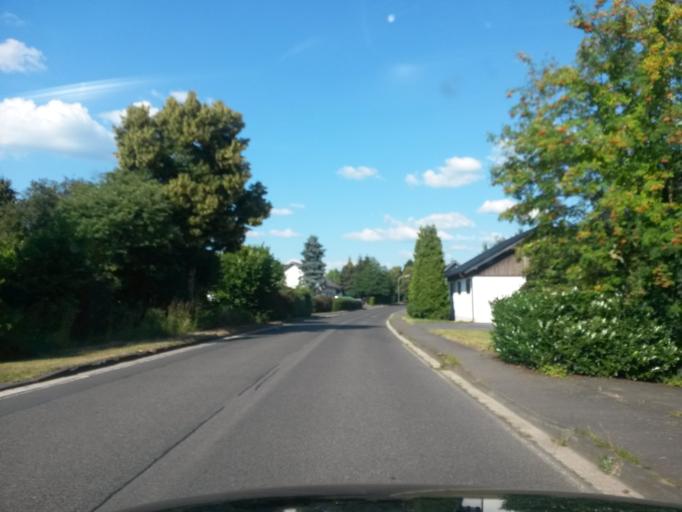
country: DE
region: North Rhine-Westphalia
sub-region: Regierungsbezirk Koln
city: Much
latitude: 50.9074
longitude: 7.3618
